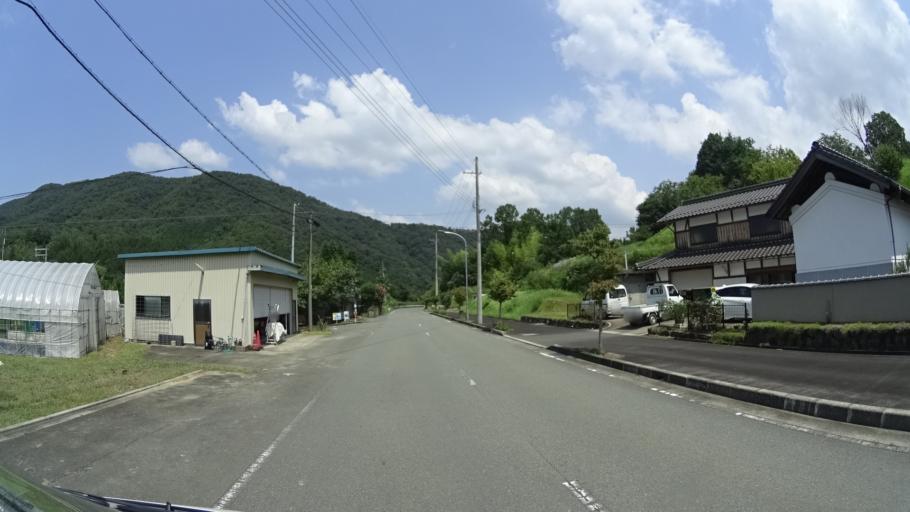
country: JP
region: Kyoto
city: Ayabe
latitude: 35.2215
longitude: 135.2162
